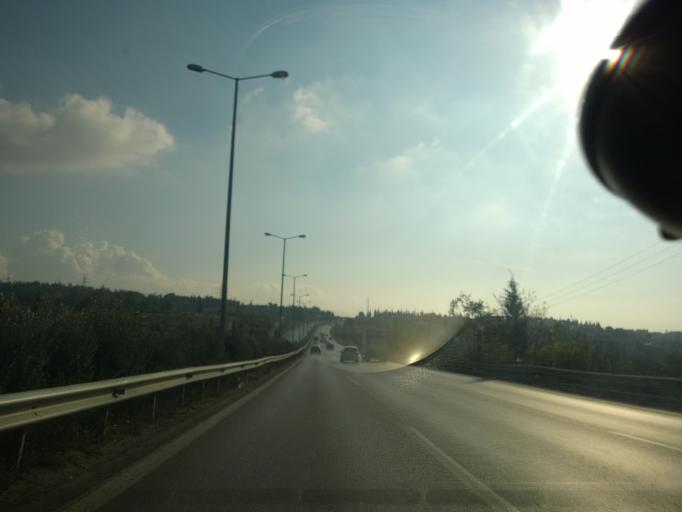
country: GR
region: Central Macedonia
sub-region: Nomos Thessalonikis
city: Pylaia
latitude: 40.6059
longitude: 22.9992
